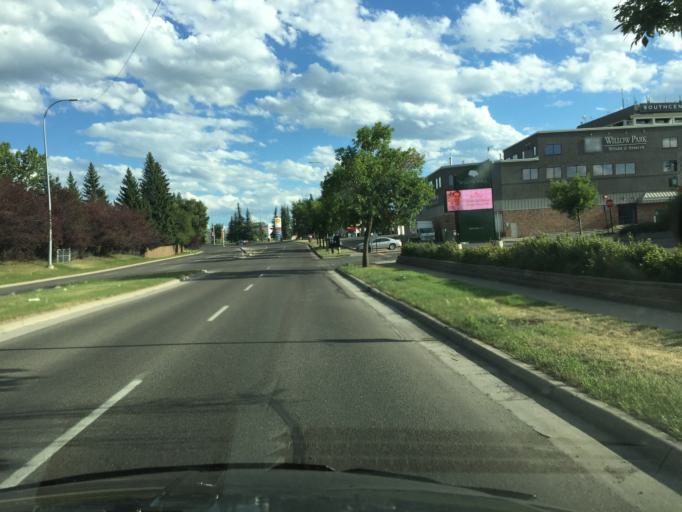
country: CA
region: Alberta
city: Calgary
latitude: 50.9568
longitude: -114.0684
